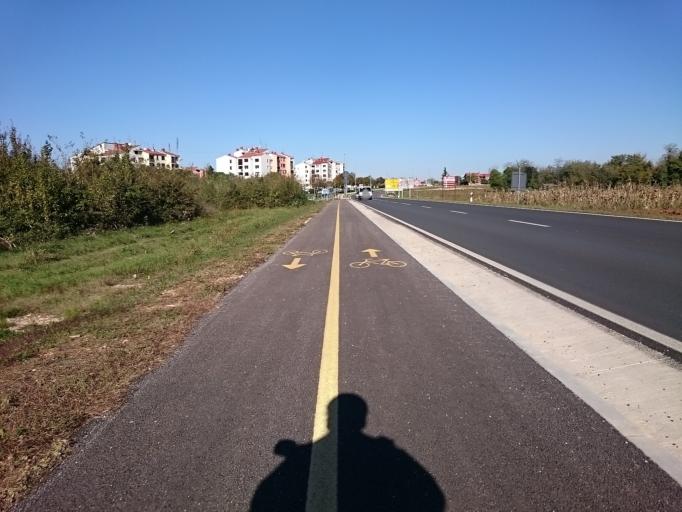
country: HR
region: Istarska
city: Umag
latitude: 45.4272
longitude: 13.5302
